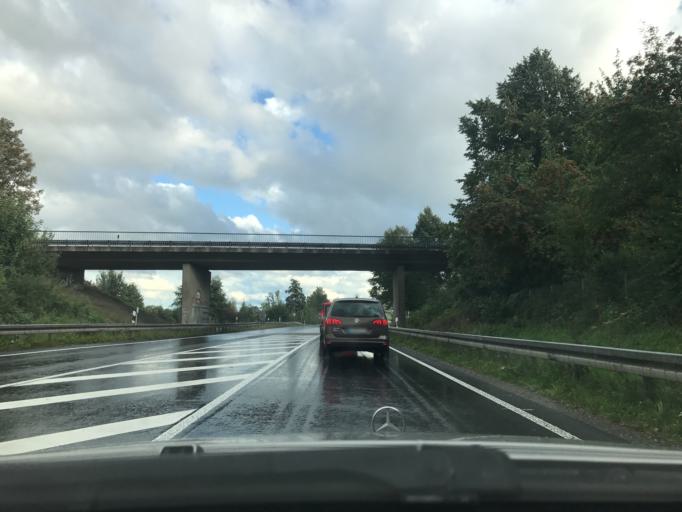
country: DE
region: North Rhine-Westphalia
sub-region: Regierungsbezirk Arnsberg
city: Bad Sassendorf
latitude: 51.5556
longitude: 8.1561
